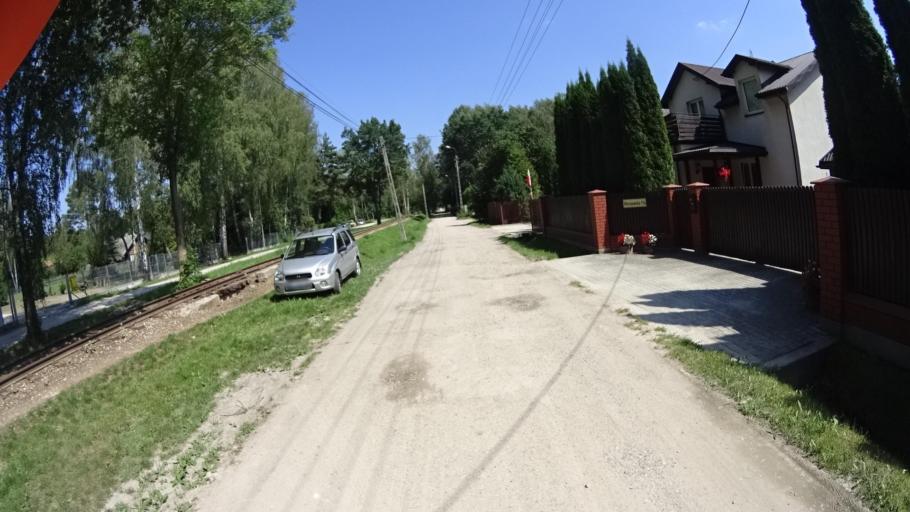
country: PL
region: Masovian Voivodeship
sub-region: Powiat piaseczynski
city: Prazmow
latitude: 52.0064
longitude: 20.9141
